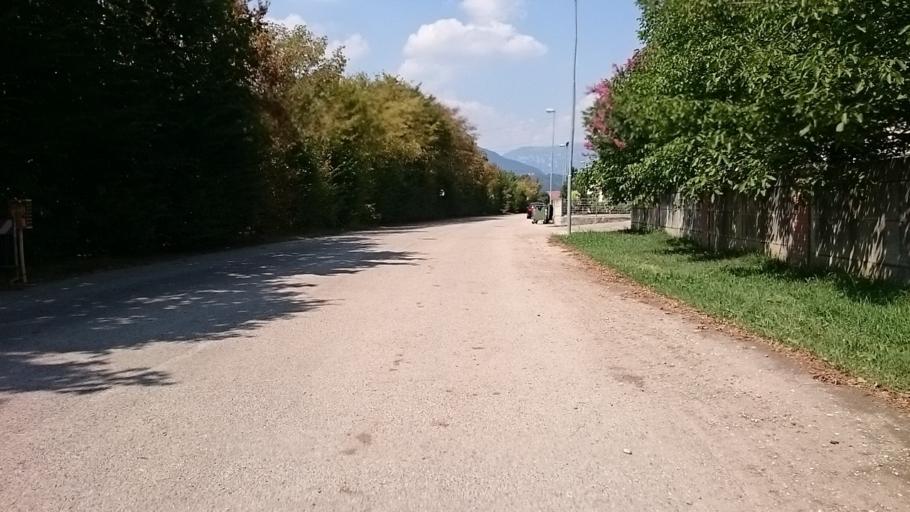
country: IT
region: Veneto
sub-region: Provincia di Vicenza
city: Bassano del Grappa
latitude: 45.7406
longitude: 11.7237
